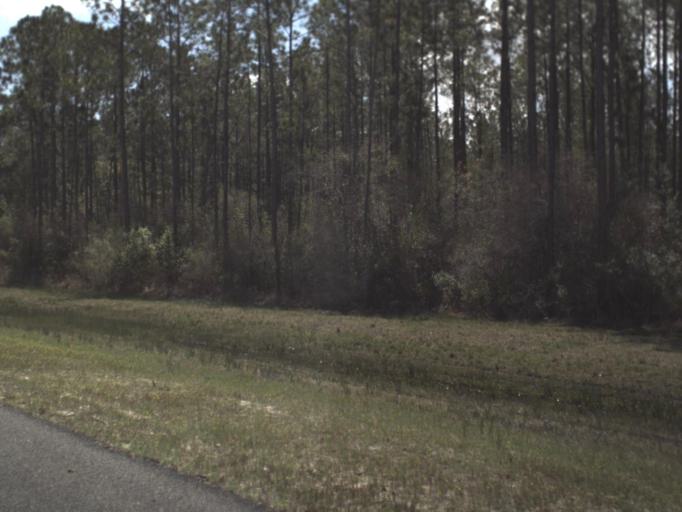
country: US
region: Florida
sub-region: Bay County
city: Laguna Beach
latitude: 30.3756
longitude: -85.8649
